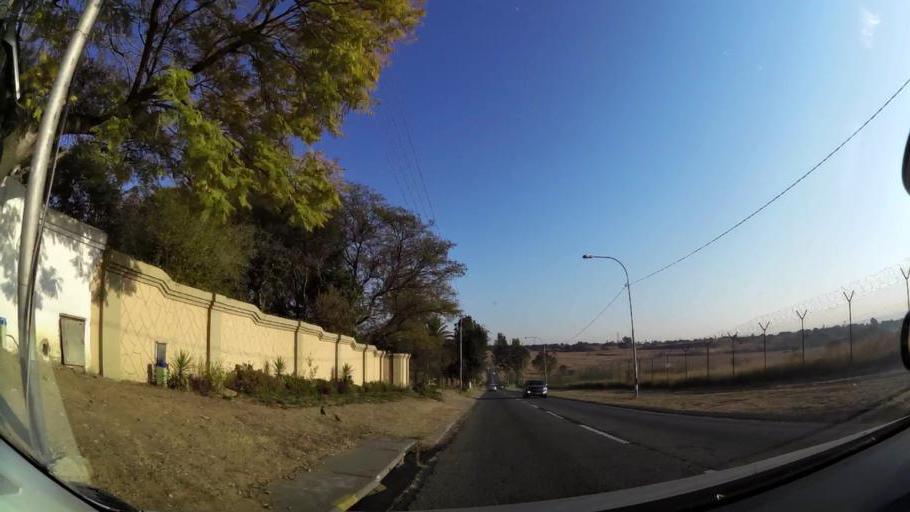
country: ZA
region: Gauteng
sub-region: City of Johannesburg Metropolitan Municipality
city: Modderfontein
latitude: -26.0733
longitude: 28.0977
